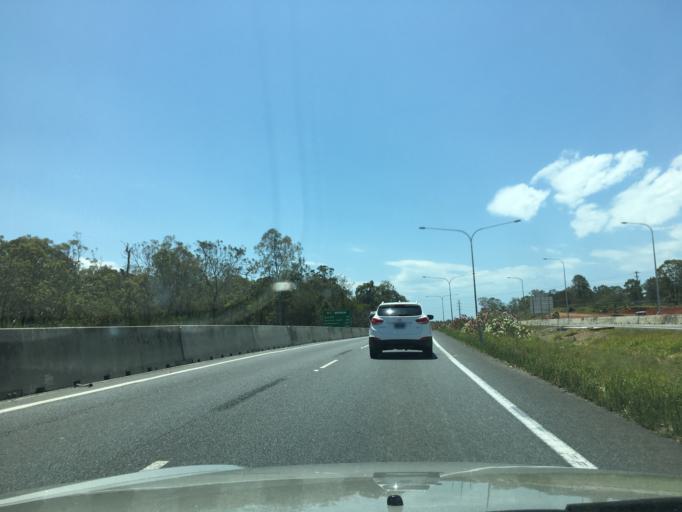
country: AU
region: Queensland
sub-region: Brisbane
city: Shorncliffe
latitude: -27.3716
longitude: 153.0964
